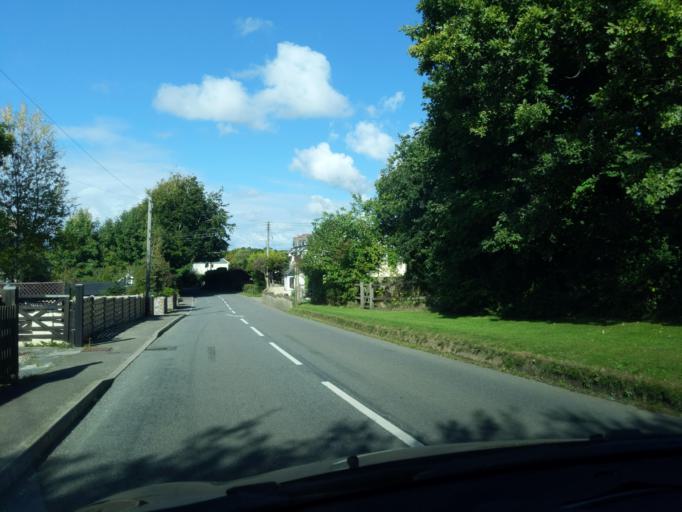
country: GB
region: England
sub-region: Devon
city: Holsworthy
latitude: 50.7675
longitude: -4.3365
